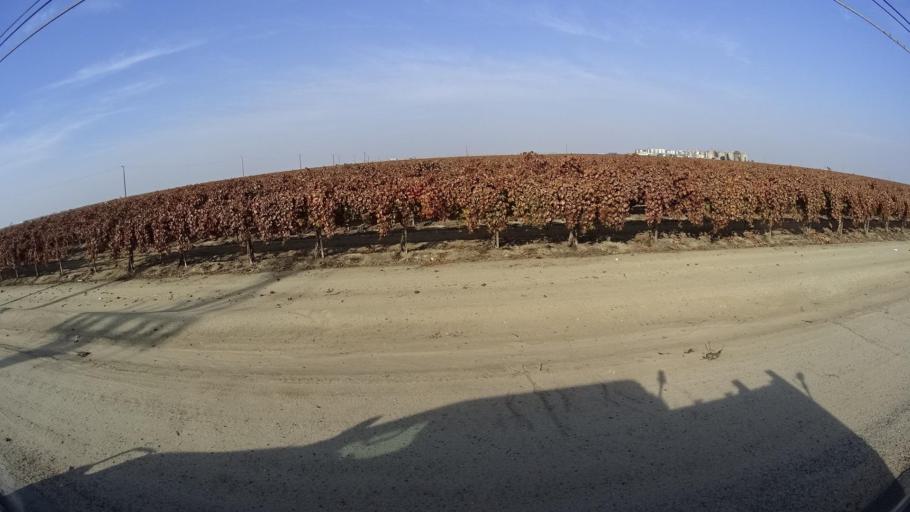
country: US
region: California
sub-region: Kern County
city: Delano
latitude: 35.7758
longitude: -119.1954
